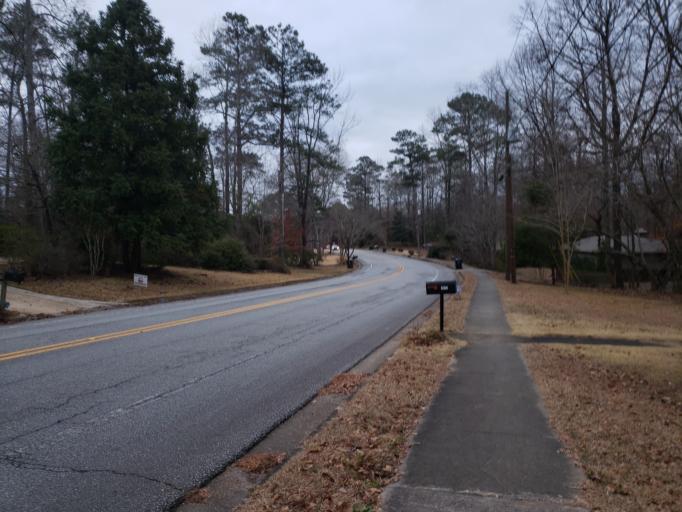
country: US
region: Alabama
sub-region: Lee County
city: Auburn
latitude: 32.5988
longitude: -85.4553
